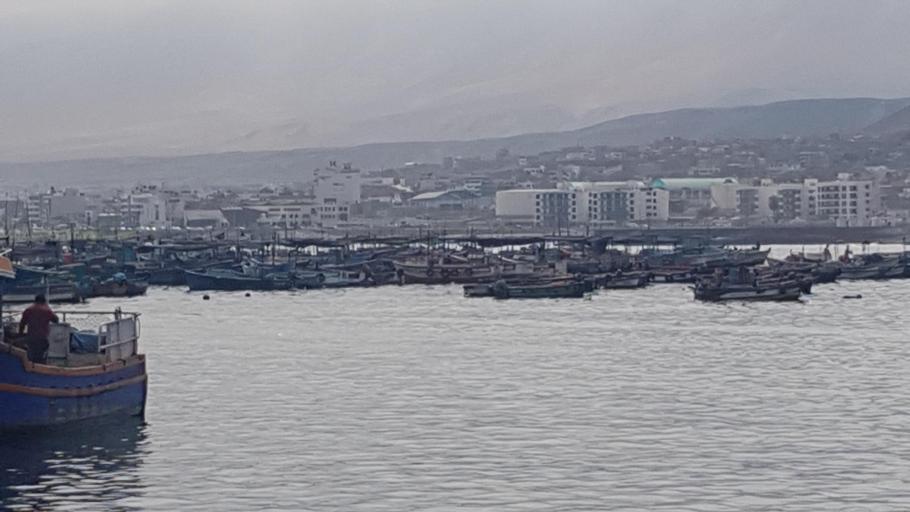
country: PE
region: Moquegua
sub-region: Provincia de Ilo
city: Ilo
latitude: -17.6441
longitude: -71.3465
